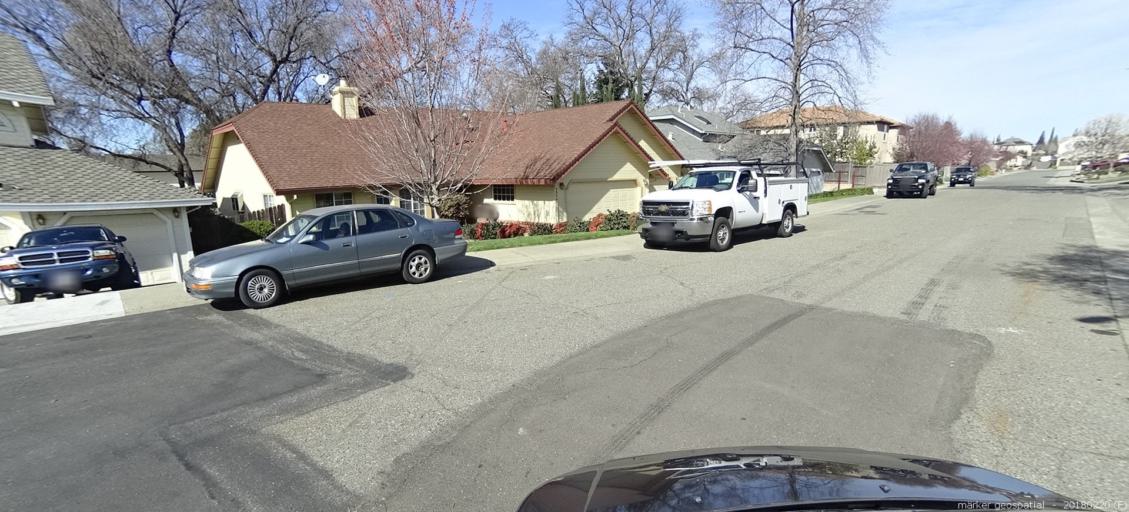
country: US
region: California
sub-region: Sacramento County
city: Orangevale
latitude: 38.6743
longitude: -121.2191
